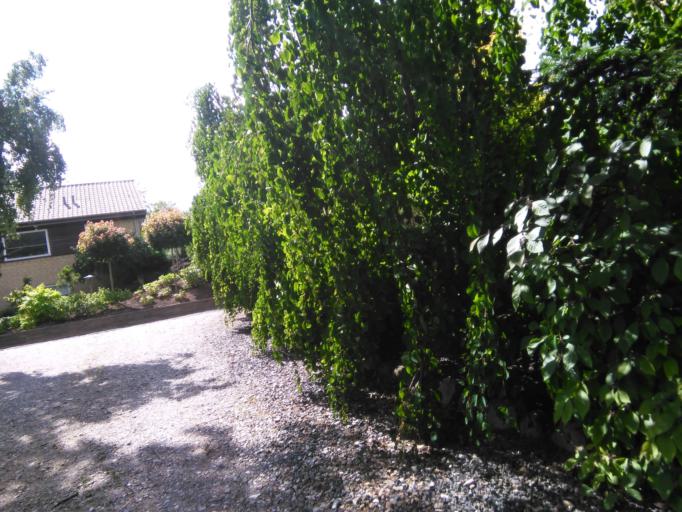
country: DK
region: Central Jutland
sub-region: Arhus Kommune
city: Arhus
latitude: 56.1118
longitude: 10.2166
